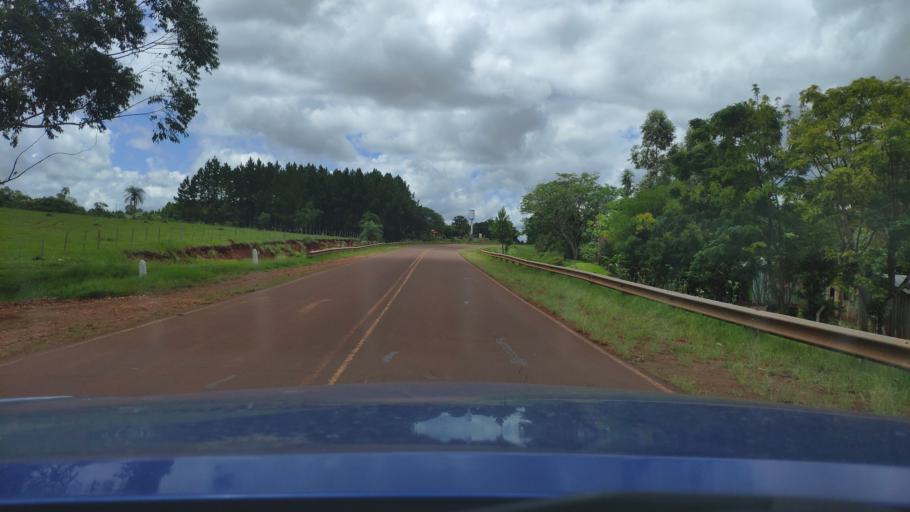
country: AR
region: Misiones
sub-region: Departamento de San Javier
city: San Javier
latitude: -27.8579
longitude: -55.2524
